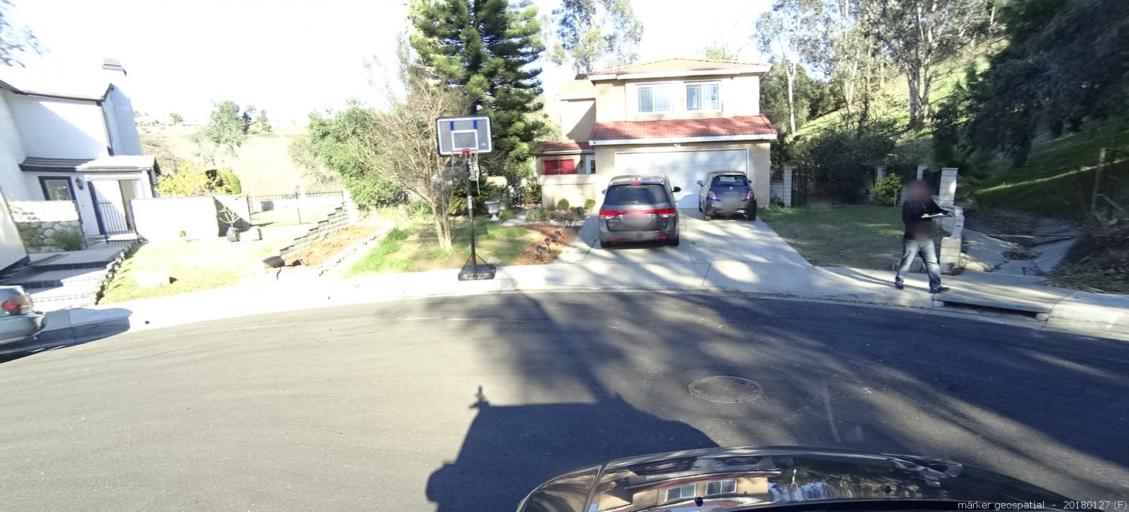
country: US
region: California
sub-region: Los Angeles County
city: Diamond Bar
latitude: 34.0246
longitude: -117.7906
